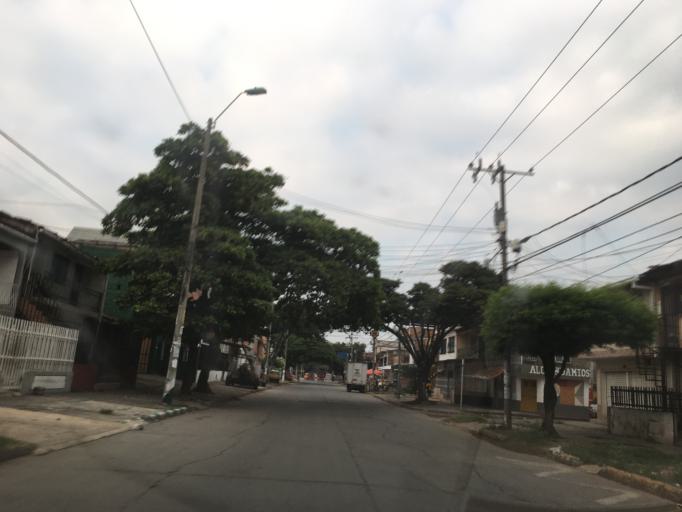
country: CO
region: Valle del Cauca
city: Cali
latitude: 3.4134
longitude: -76.5226
